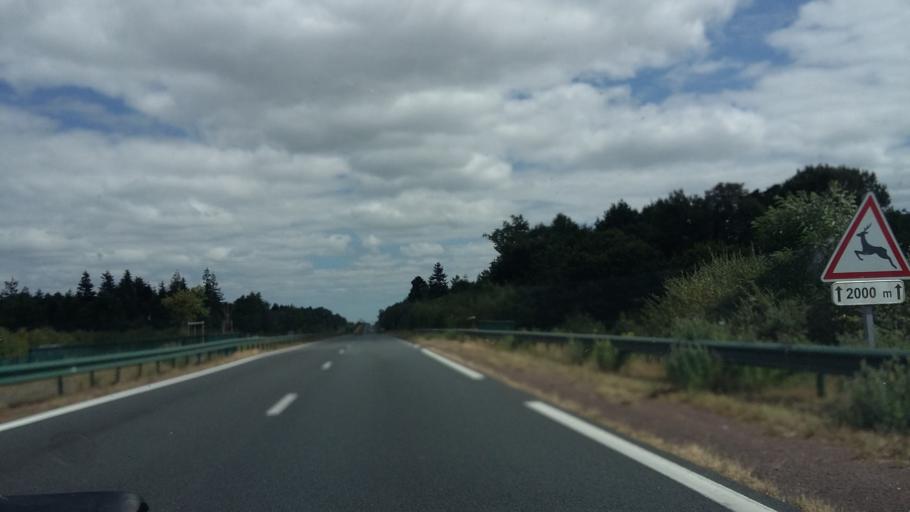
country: FR
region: Pays de la Loire
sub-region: Departement de la Vendee
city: Bournezeau
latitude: 46.6509
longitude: -1.2234
